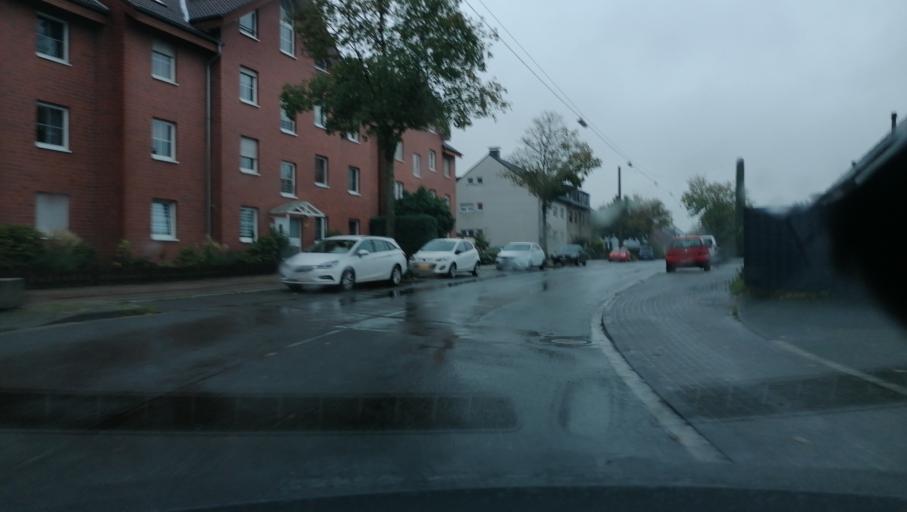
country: DE
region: North Rhine-Westphalia
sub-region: Regierungsbezirk Arnsberg
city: Herne
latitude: 51.5858
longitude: 7.2534
